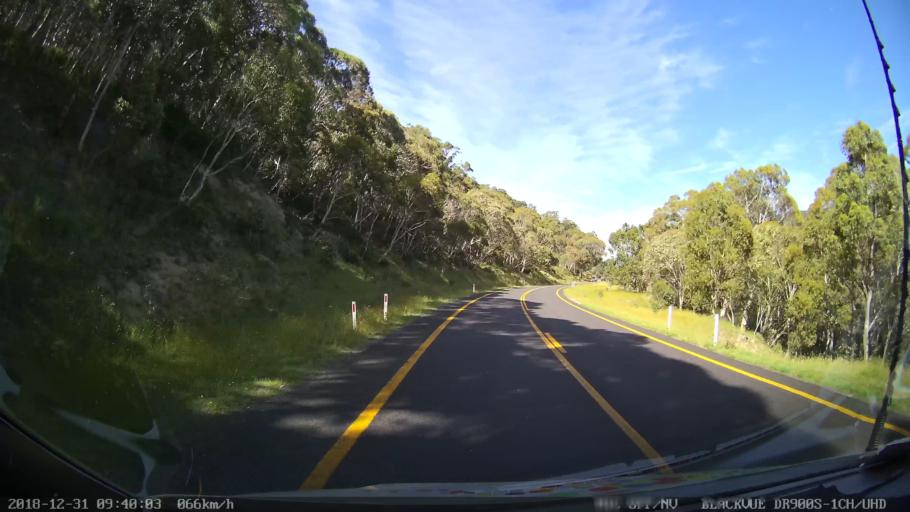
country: AU
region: New South Wales
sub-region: Snowy River
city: Jindabyne
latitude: -36.4823
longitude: 148.3486
